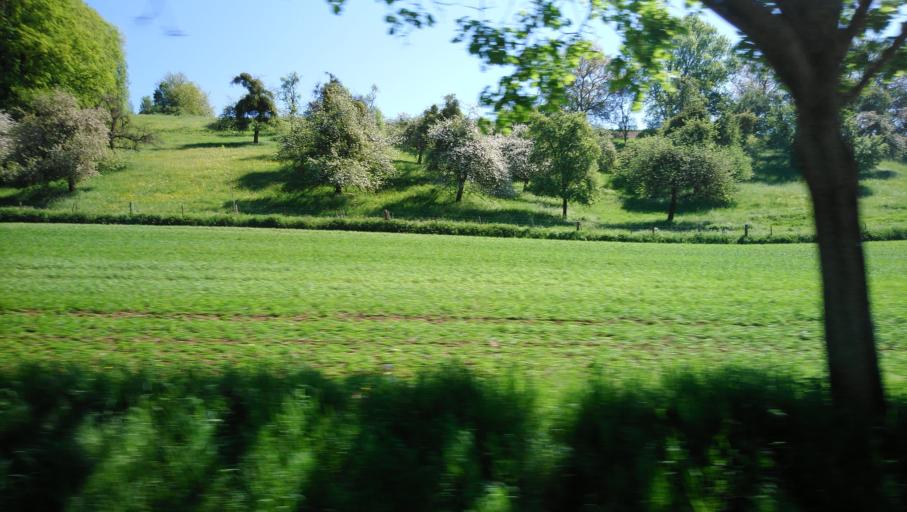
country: LU
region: Diekirch
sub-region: Canton de Vianden
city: Tandel
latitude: 49.8746
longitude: 6.1902
